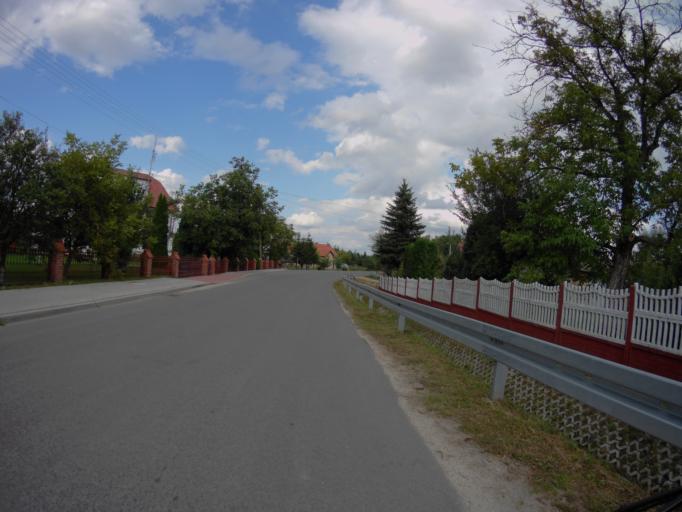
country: PL
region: Subcarpathian Voivodeship
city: Nowa Sarzyna
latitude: 50.2864
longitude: 22.3507
